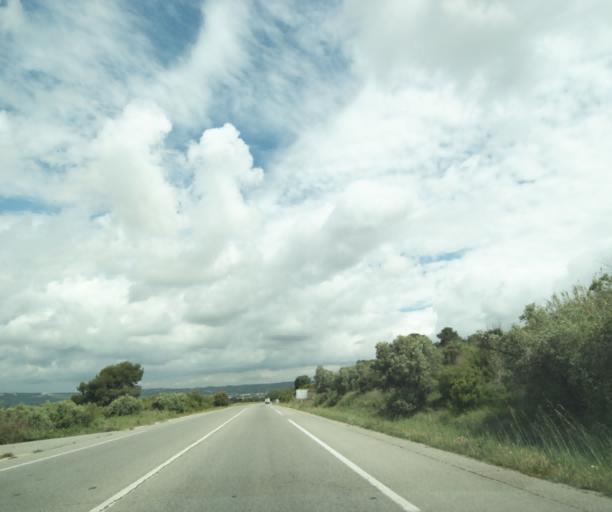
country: FR
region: Provence-Alpes-Cote d'Azur
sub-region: Departement des Bouches-du-Rhone
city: La Fare-les-Oliviers
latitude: 43.5222
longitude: 5.1980
